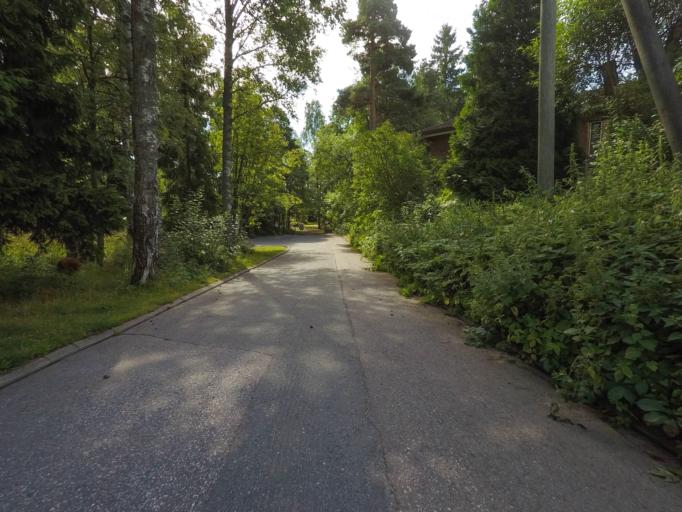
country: FI
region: Uusimaa
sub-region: Helsinki
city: Helsinki
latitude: 60.1603
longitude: 25.0562
